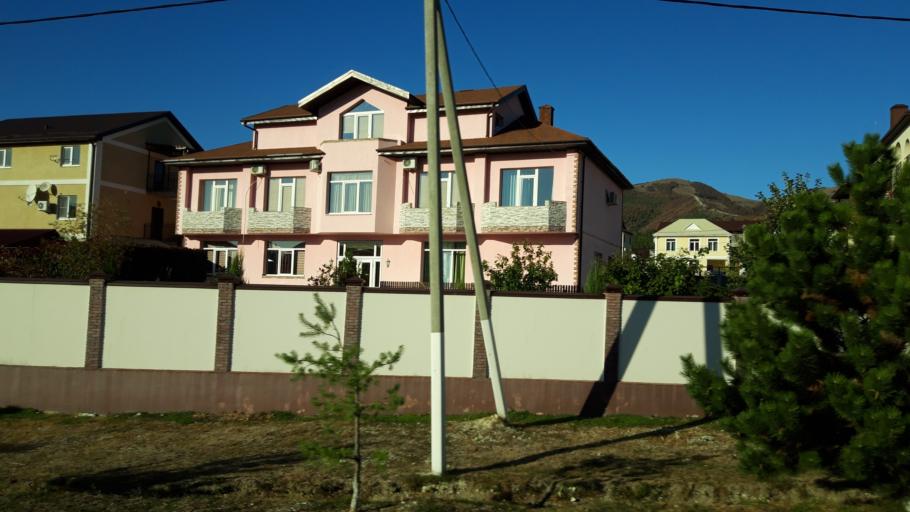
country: RU
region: Krasnodarskiy
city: Kabardinka
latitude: 44.6459
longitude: 37.9573
